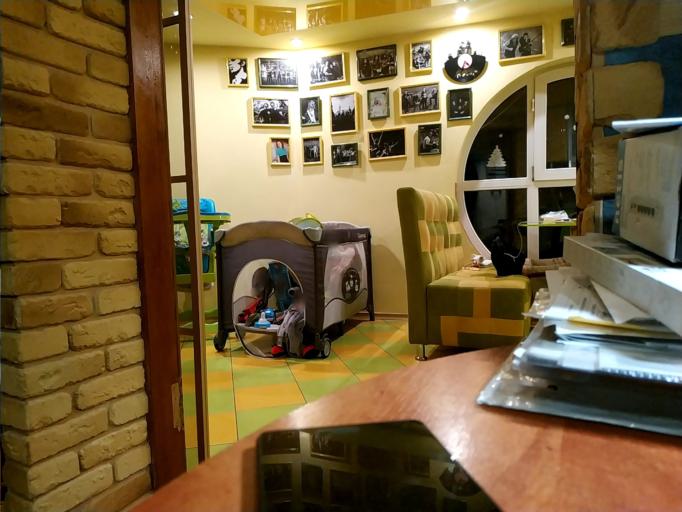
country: RU
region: Orjol
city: Naryshkino
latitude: 53.0485
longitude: 35.6788
